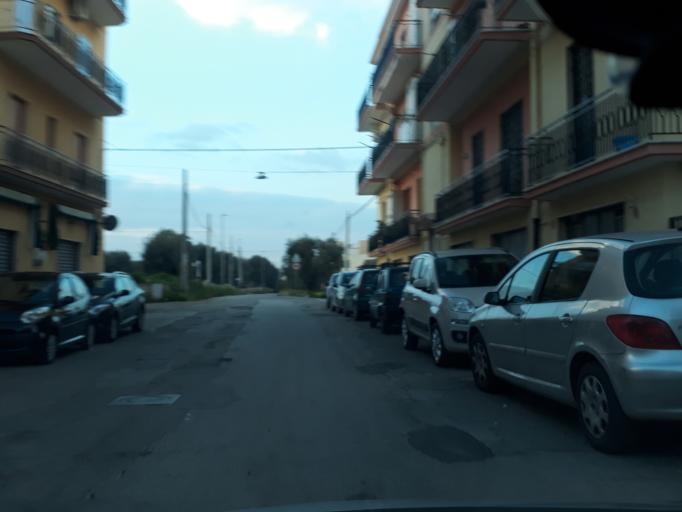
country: IT
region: Apulia
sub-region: Provincia di Brindisi
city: Fasano
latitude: 40.8390
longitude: 17.3554
